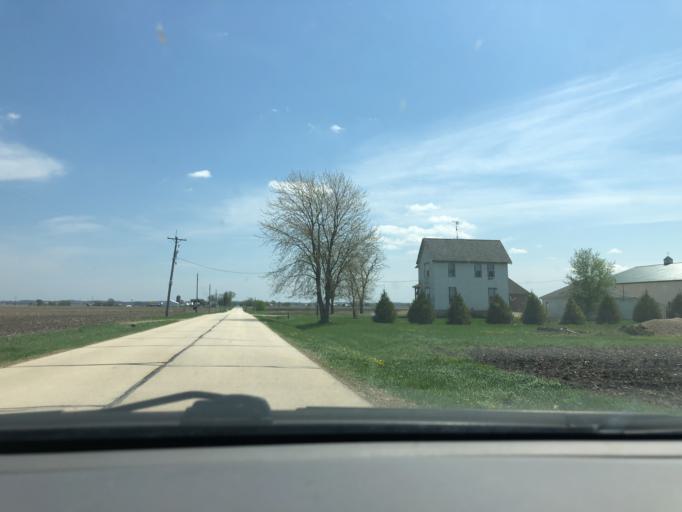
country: US
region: Illinois
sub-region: Kane County
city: Hampshire
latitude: 42.1100
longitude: -88.5944
